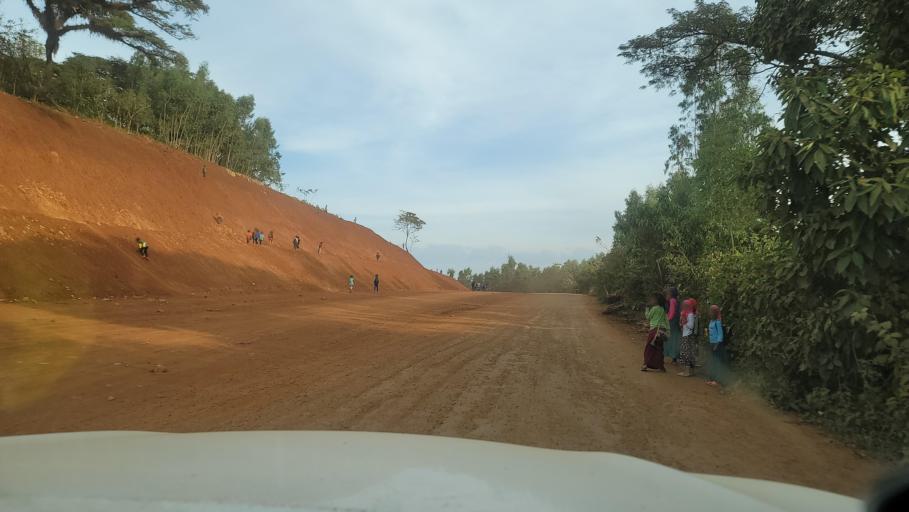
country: ET
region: Oromiya
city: Agaro
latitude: 7.8172
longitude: 36.5204
